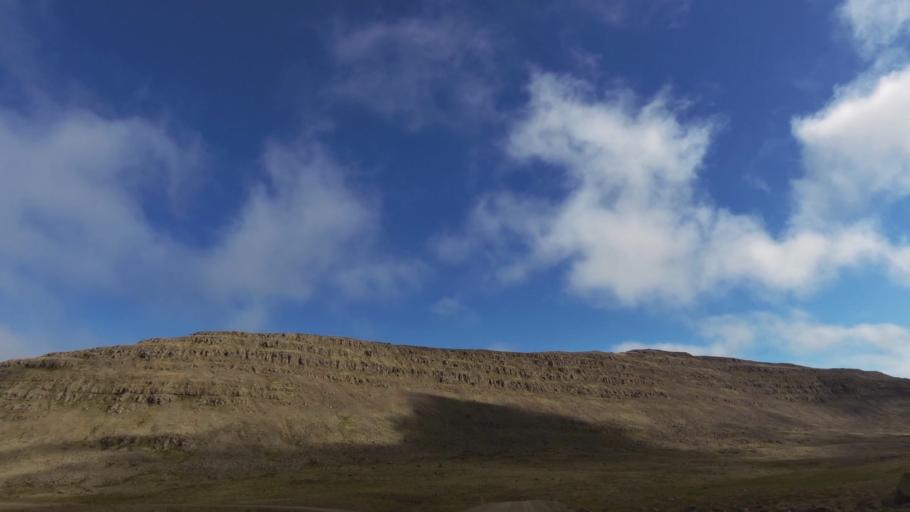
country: IS
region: West
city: Olafsvik
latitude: 65.5773
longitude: -24.0852
